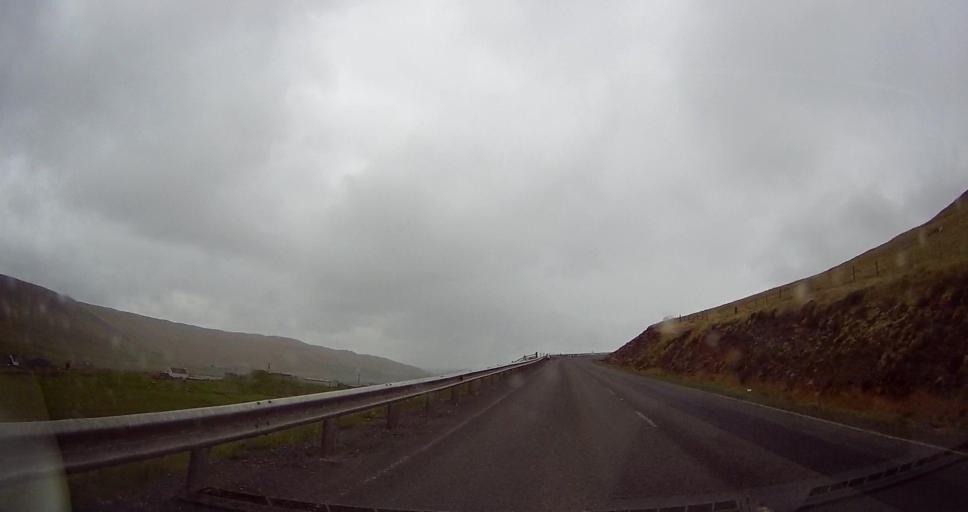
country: GB
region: Scotland
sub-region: Shetland Islands
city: Lerwick
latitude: 60.2494
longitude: -1.3013
